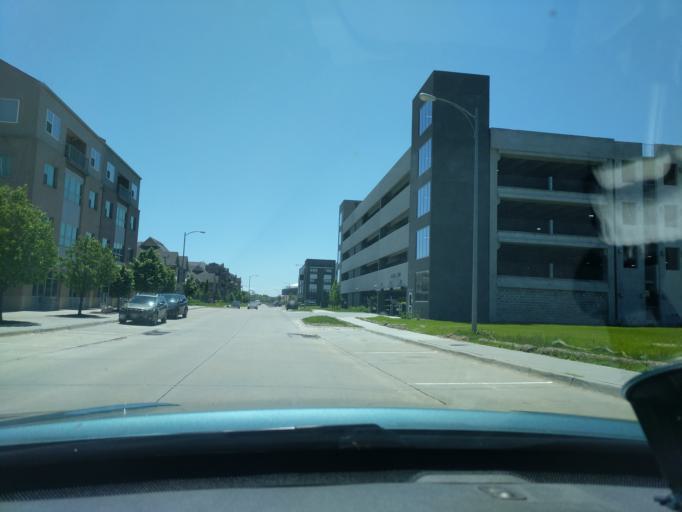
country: US
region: Nebraska
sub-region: Douglas County
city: Ralston
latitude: 41.2412
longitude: -96.0121
